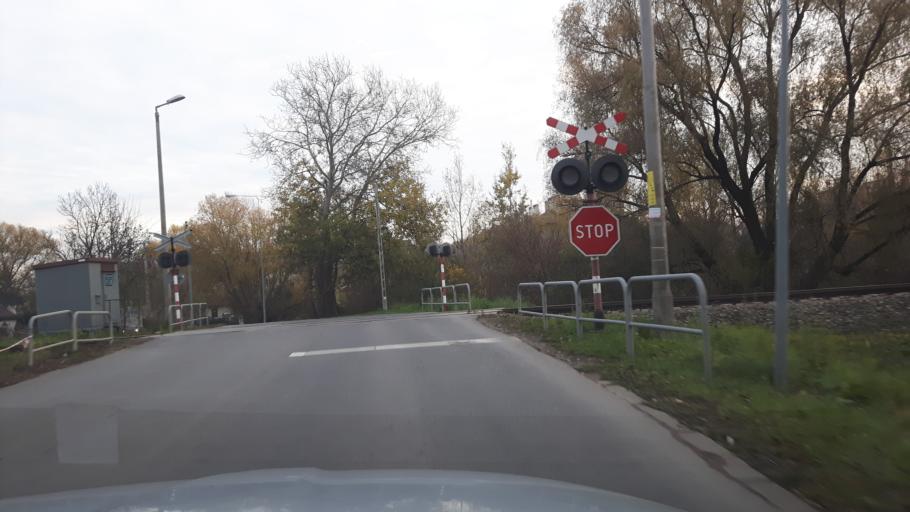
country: PL
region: Masovian Voivodeship
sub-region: Warszawa
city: Wilanow
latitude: 52.1818
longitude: 21.0988
